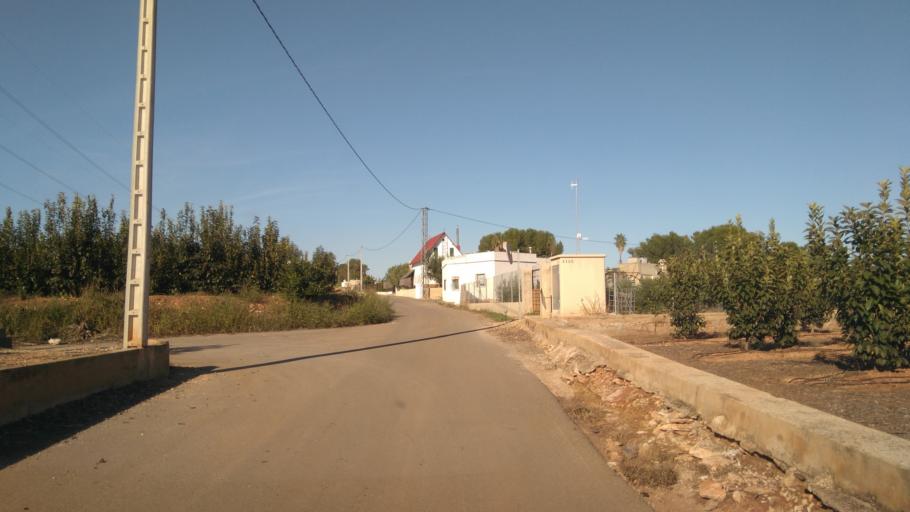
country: ES
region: Valencia
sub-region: Provincia de Valencia
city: Masalaves
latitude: 39.1760
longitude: -0.5517
